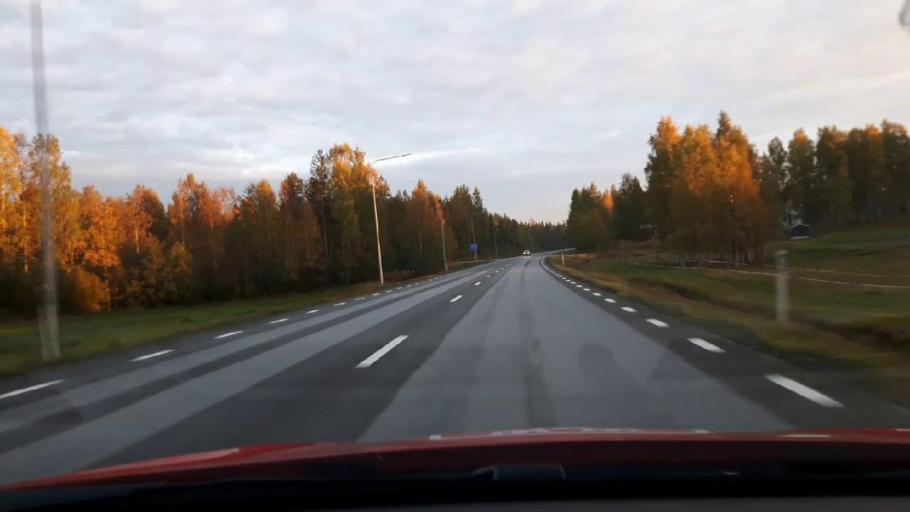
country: SE
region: Jaemtland
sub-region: OEstersunds Kommun
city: Lit
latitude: 63.3097
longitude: 14.8704
